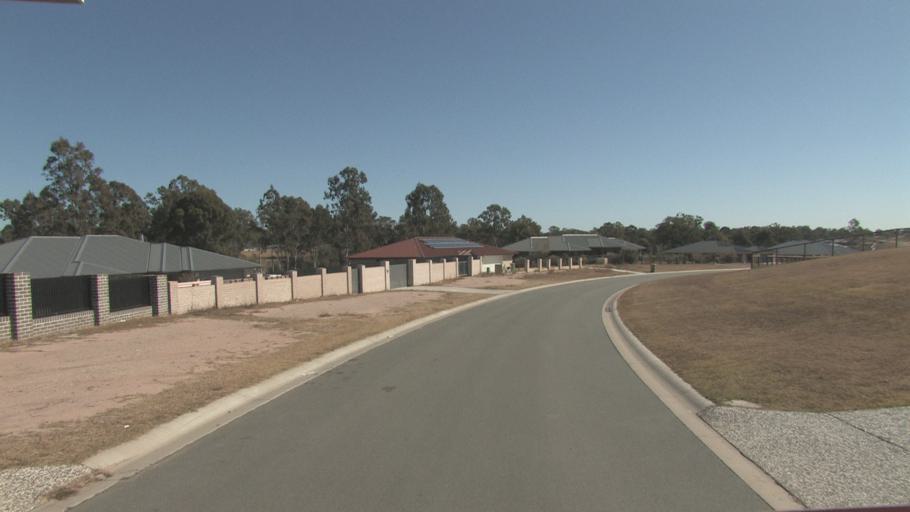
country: AU
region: Queensland
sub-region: Logan
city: Cedar Vale
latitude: -27.8674
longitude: 153.0463
